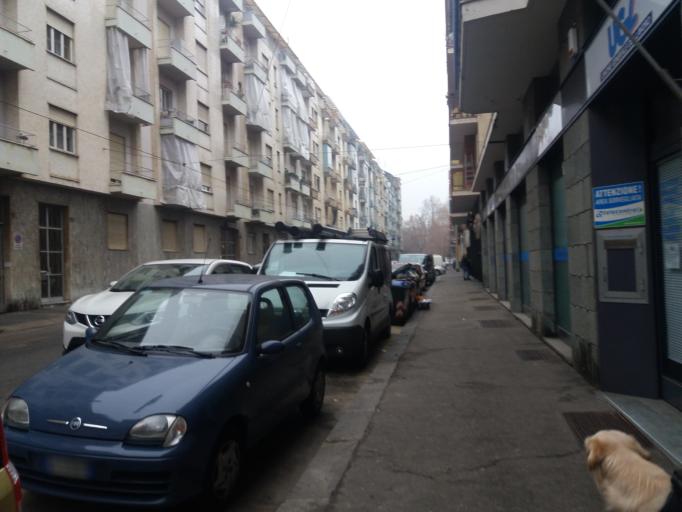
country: IT
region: Piedmont
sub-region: Provincia di Torino
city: Lesna
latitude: 45.0630
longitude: 7.6206
